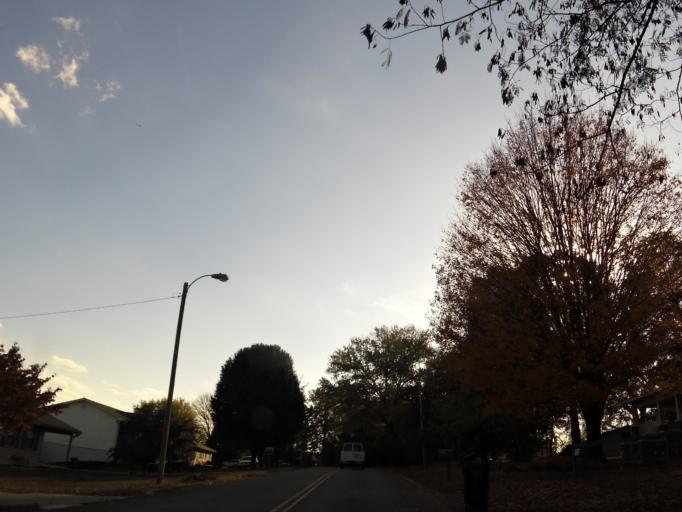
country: US
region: Tennessee
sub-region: Anderson County
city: Clinton
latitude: 36.1168
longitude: -84.1202
